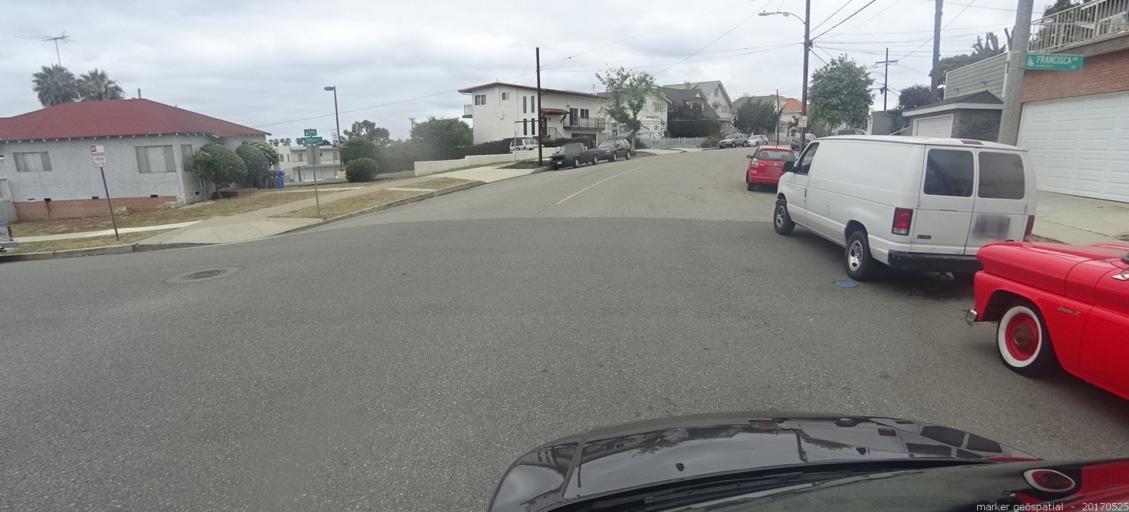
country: US
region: California
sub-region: Los Angeles County
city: Redondo Beach
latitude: 33.8429
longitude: -118.3843
